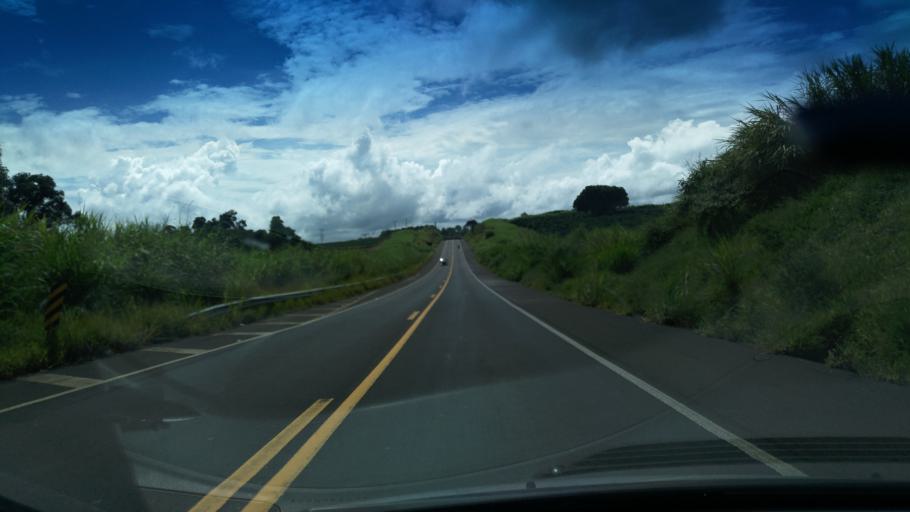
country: BR
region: Sao Paulo
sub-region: Santo Antonio Do Jardim
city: Espirito Santo do Pinhal
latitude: -22.1459
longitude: -46.7161
